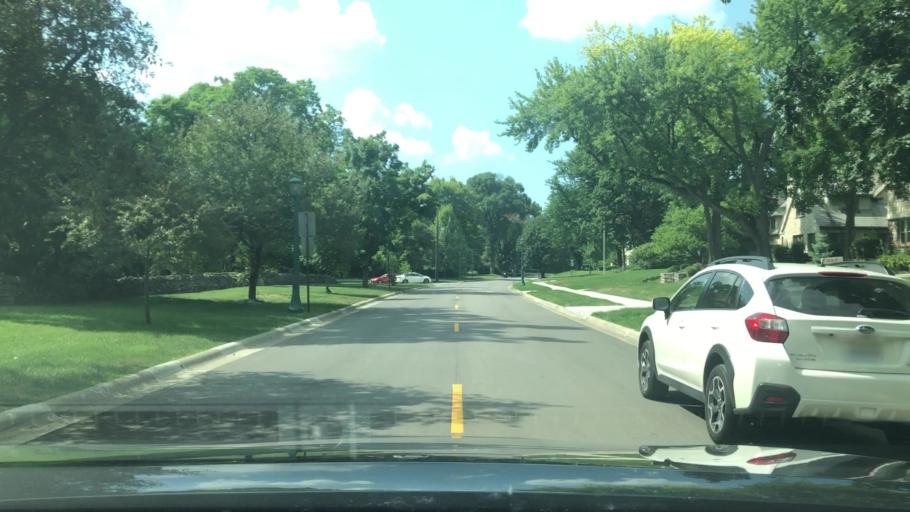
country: US
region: Ohio
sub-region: Franklin County
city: Upper Arlington
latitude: 40.0025
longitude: -83.0679
